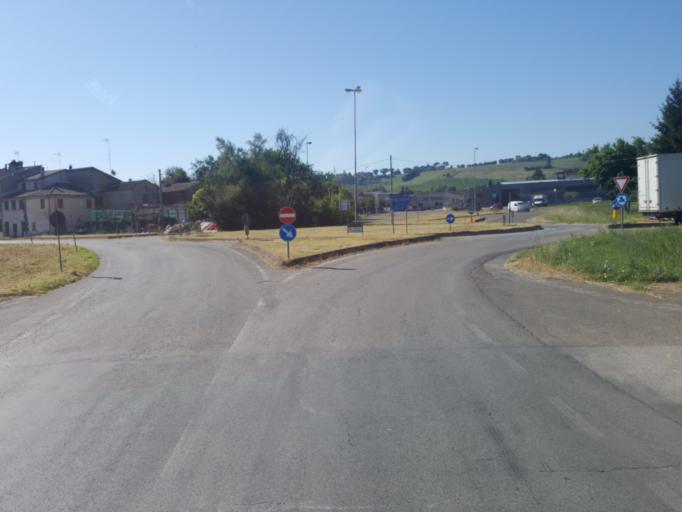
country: IT
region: The Marches
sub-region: Provincia di Pesaro e Urbino
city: Padiglione
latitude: 43.8376
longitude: 12.7252
